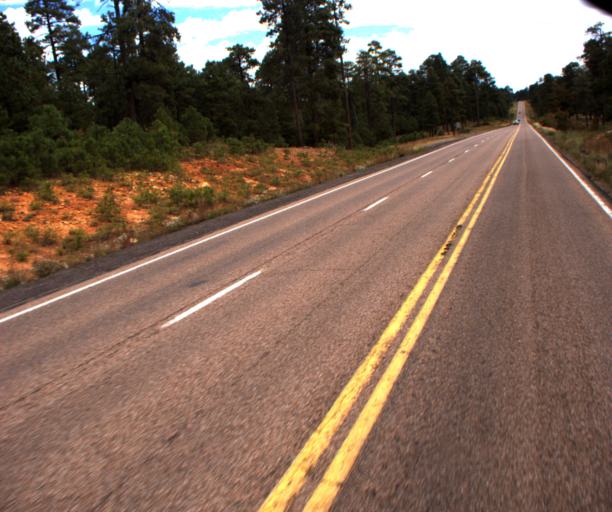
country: US
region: Arizona
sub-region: Navajo County
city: Heber-Overgaard
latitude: 34.3357
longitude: -110.7436
